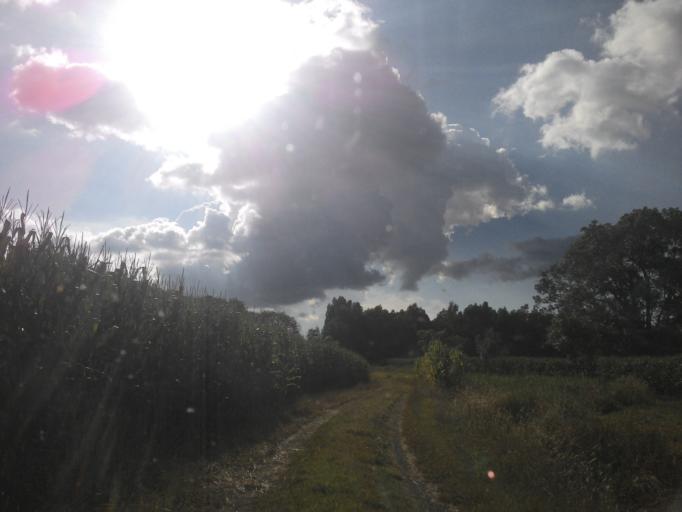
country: MX
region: Jalisco
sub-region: Atotonilco el Alto
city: Ojo de Agua de Moran
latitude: 20.6085
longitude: -102.4702
